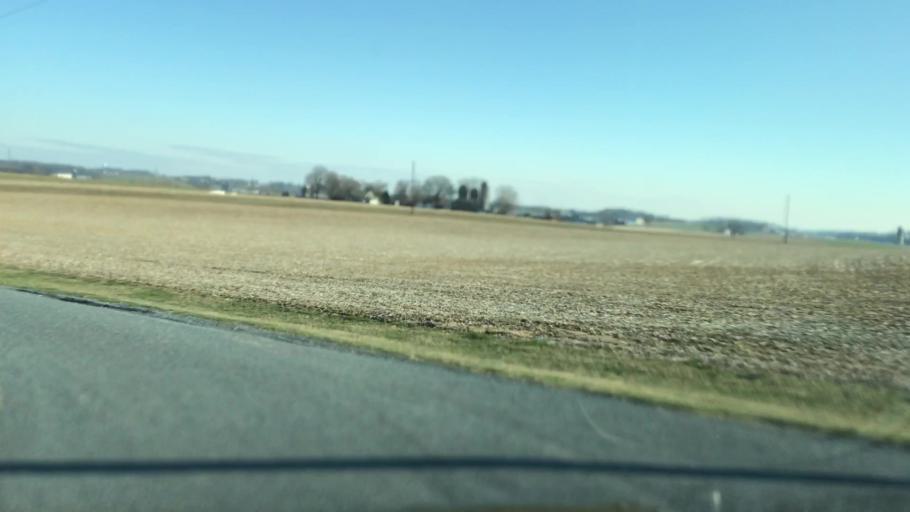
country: US
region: Pennsylvania
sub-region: Lancaster County
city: Maytown
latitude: 40.0976
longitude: -76.6124
